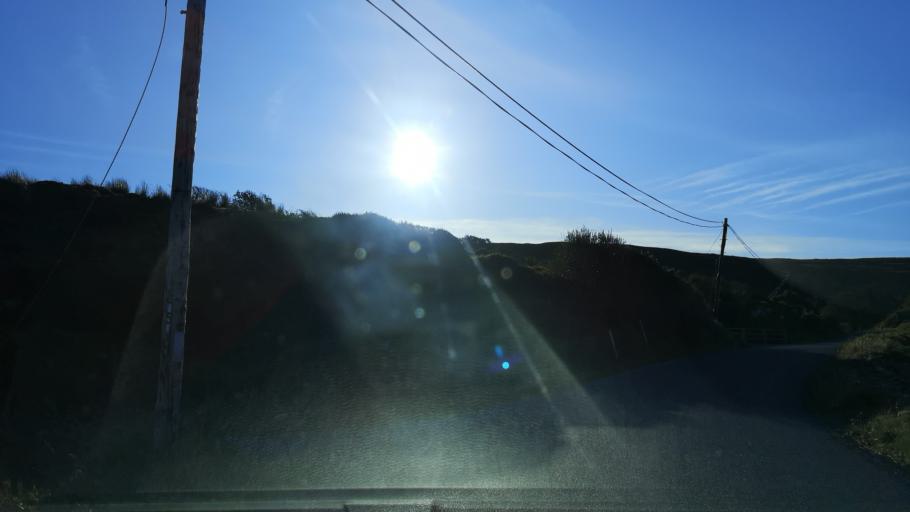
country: IE
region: Connaught
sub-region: County Galway
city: Clifden
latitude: 53.5040
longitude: -10.0526
